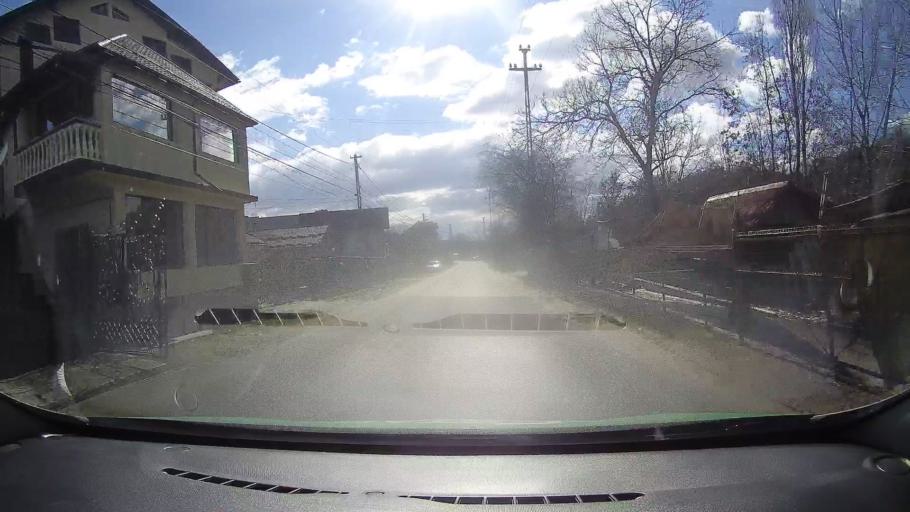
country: RO
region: Dambovita
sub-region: Comuna Runcu
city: Badeni
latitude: 45.1544
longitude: 25.3998
